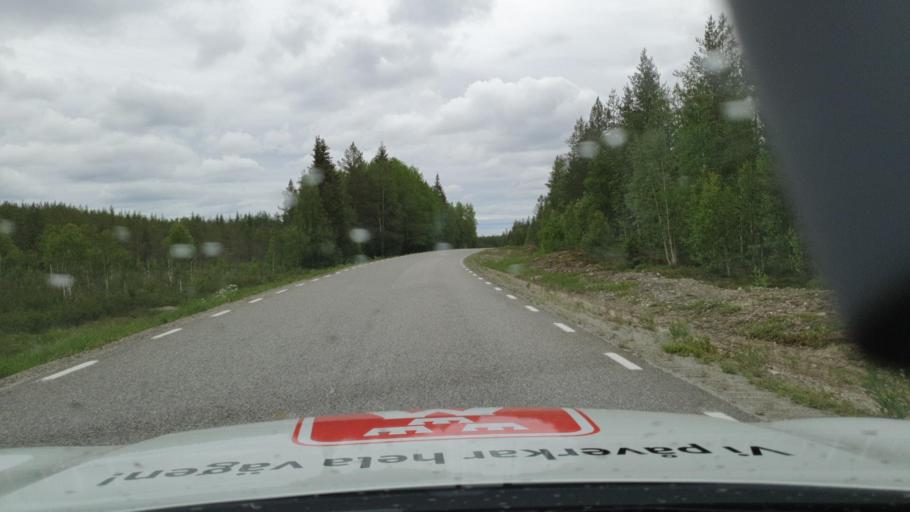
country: SE
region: Vaesterbotten
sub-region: Lycksele Kommun
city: Lycksele
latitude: 64.2245
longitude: 18.2482
